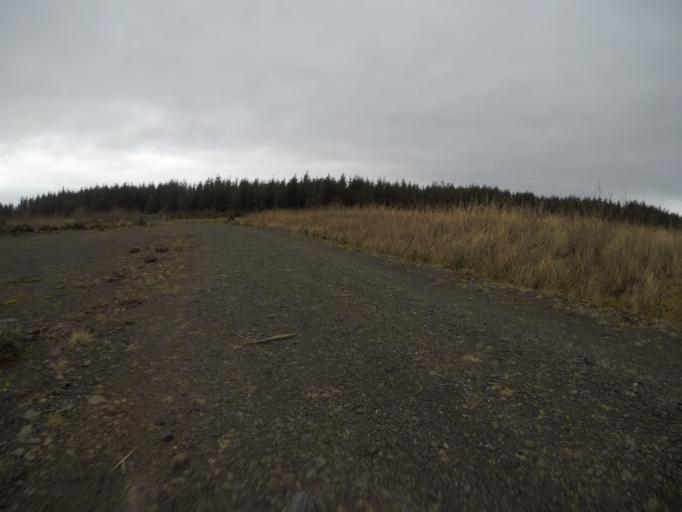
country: GB
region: Scotland
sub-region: East Ayrshire
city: Newmilns
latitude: 55.6774
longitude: -4.3554
